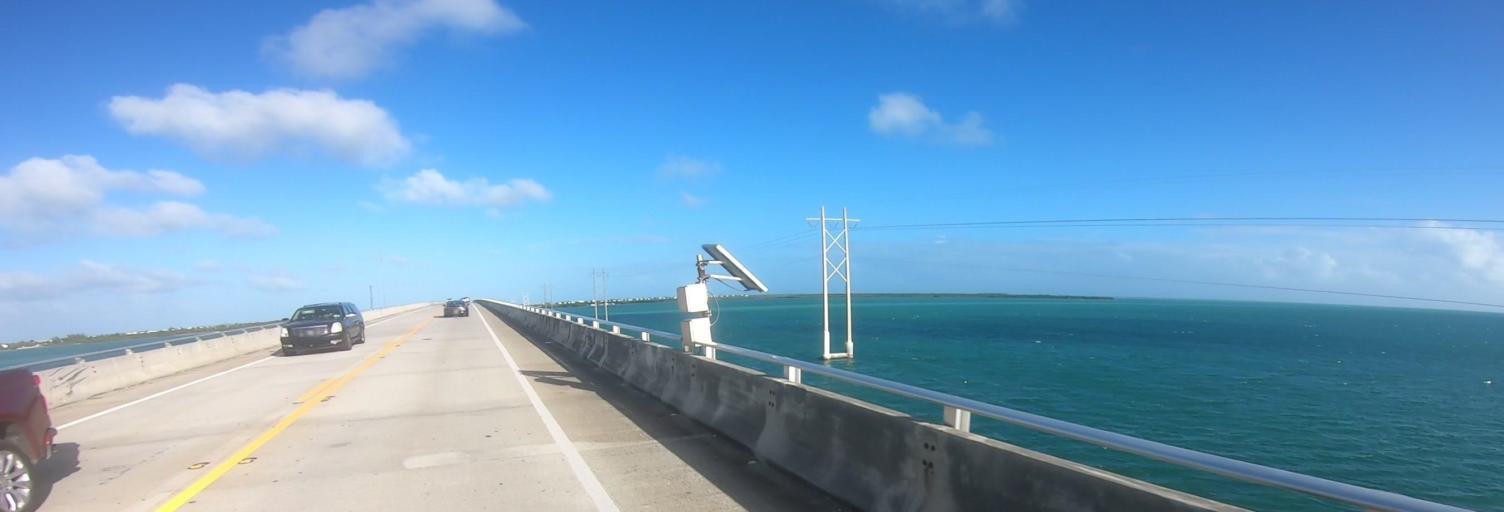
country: US
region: Florida
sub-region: Monroe County
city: Cudjoe Key
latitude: 24.6600
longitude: -81.4343
